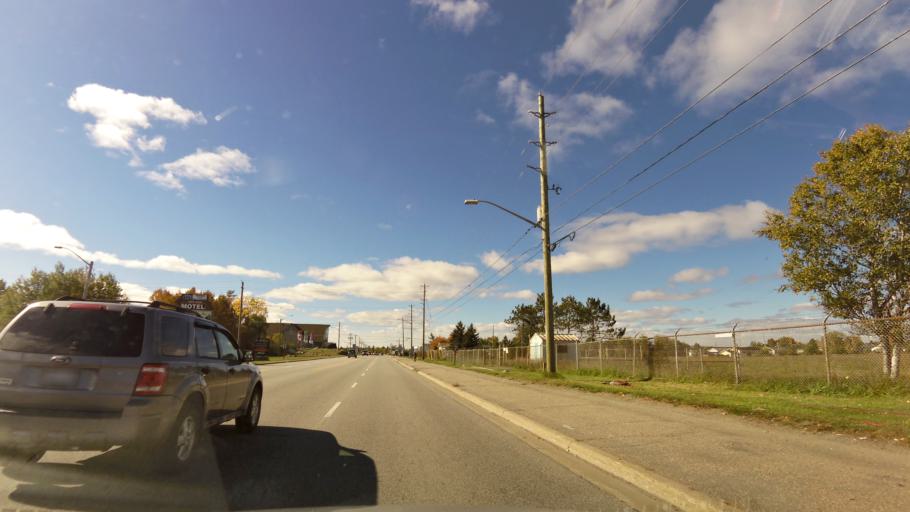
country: CA
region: Ontario
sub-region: Nipissing District
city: North Bay
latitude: 46.3662
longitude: -79.9359
